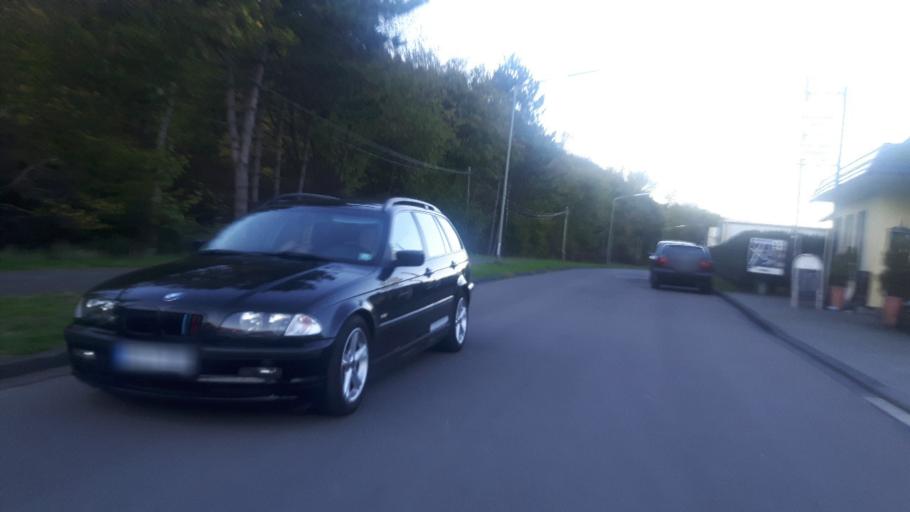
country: DE
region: Rheinland-Pfalz
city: Mudersbach
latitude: 50.8325
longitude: 7.9525
